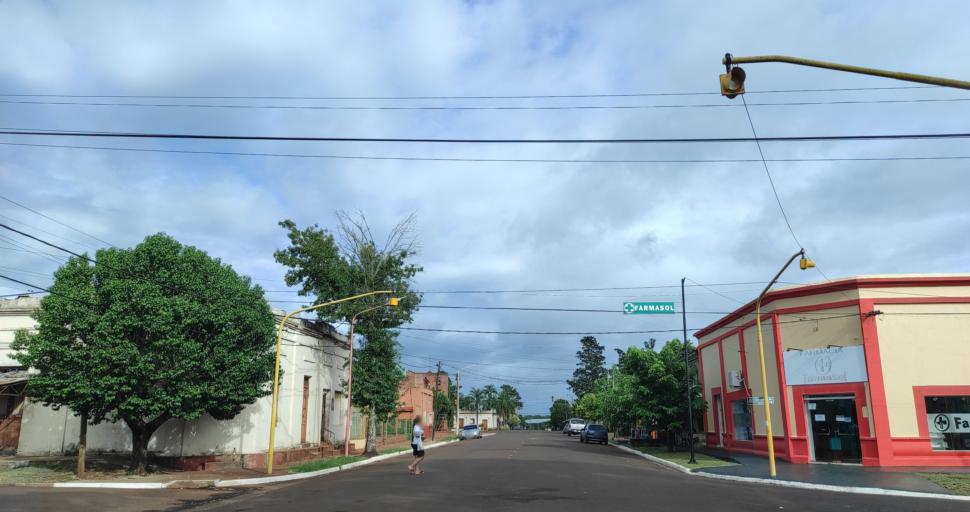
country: AR
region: Misiones
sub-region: Departamento de Apostoles
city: San Jose
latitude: -27.7687
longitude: -55.7766
